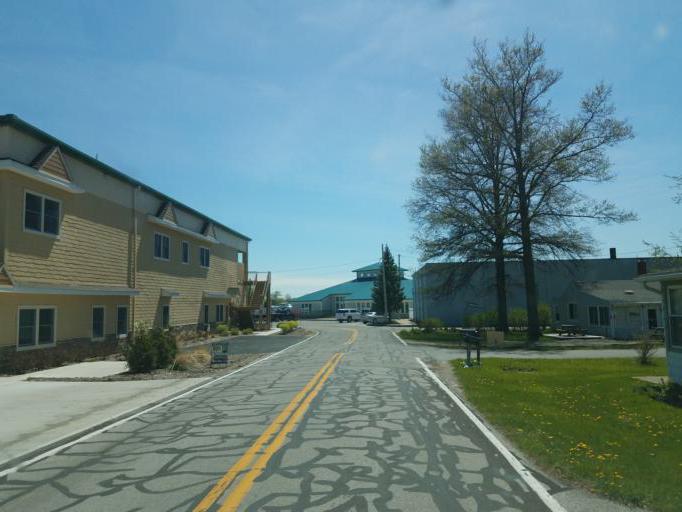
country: US
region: Ohio
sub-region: Ottawa County
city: Port Clinton
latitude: 41.5696
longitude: -82.8223
